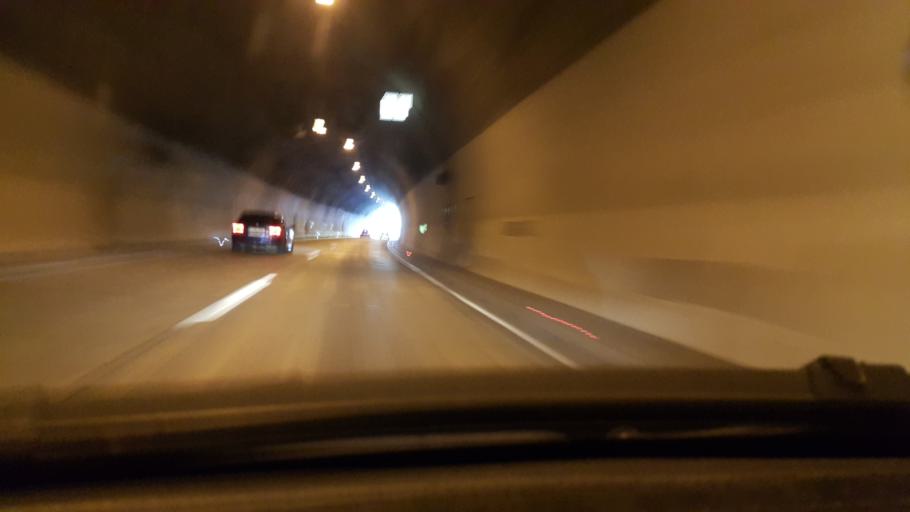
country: SI
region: Vransko
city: Vransko
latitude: 46.2123
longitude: 14.9128
